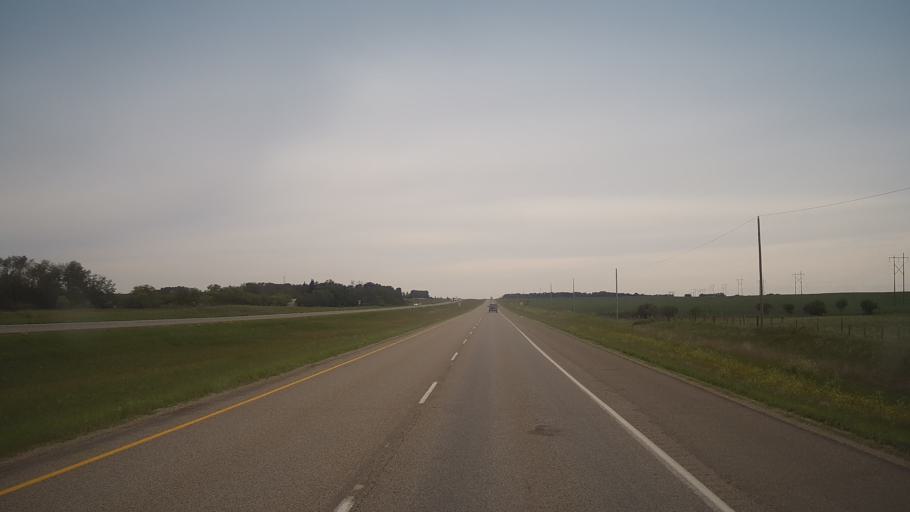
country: CA
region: Saskatchewan
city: Saskatoon
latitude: 51.8948
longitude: -106.5184
